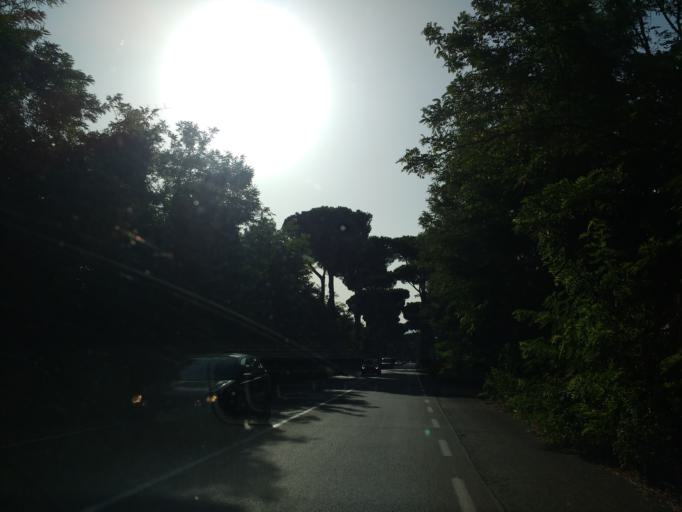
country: IT
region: Latium
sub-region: Citta metropolitana di Roma Capitale
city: Marino
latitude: 41.7540
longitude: 12.6346
